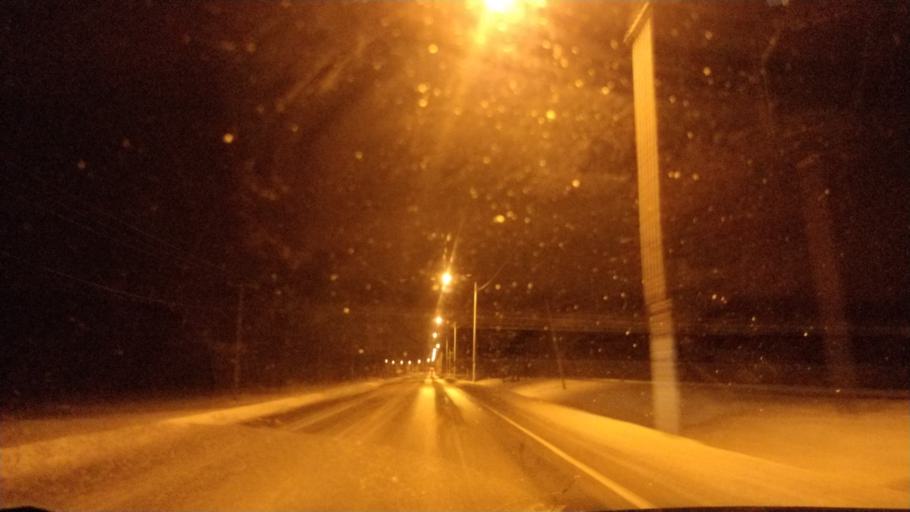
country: FI
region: Lapland
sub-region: Rovaniemi
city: Rovaniemi
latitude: 66.3066
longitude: 25.3584
